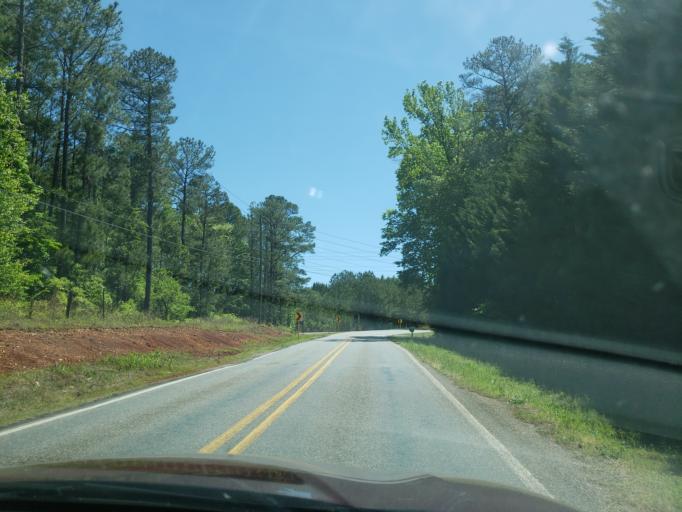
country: US
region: Alabama
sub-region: Tallapoosa County
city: Dadeville
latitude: 32.7079
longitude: -85.8271
